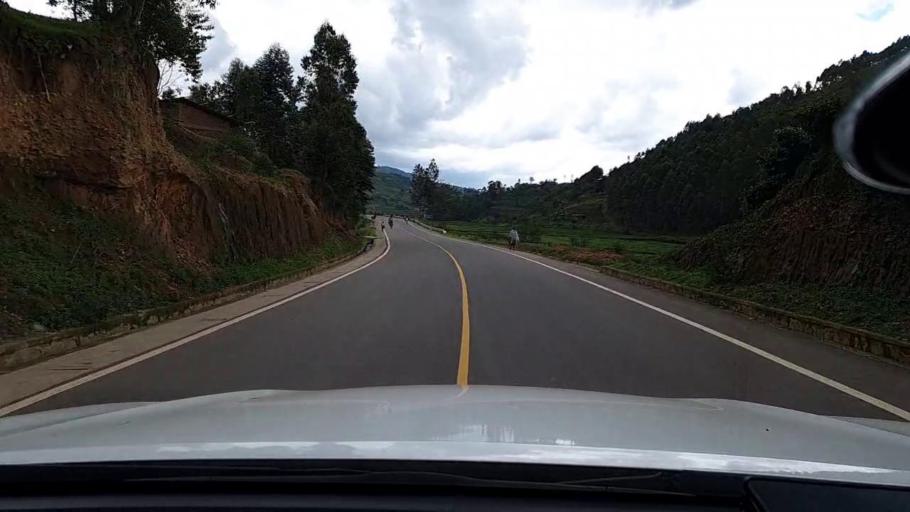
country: RW
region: Northern Province
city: Byumba
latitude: -1.6544
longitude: 29.9107
